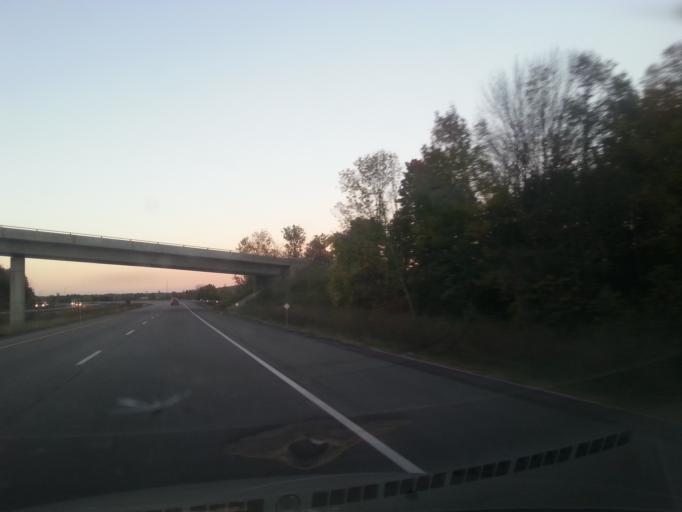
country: CA
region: Ontario
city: Orillia
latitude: 44.6611
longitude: -79.6439
